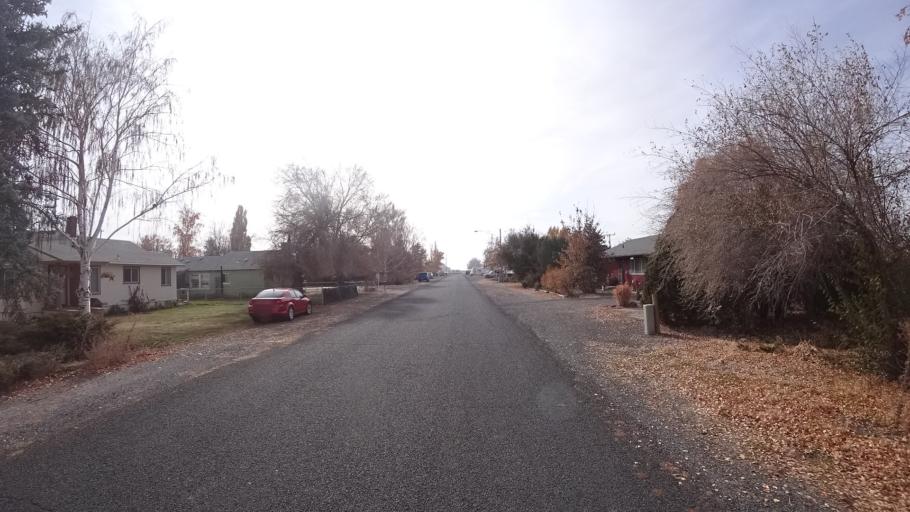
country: US
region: California
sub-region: Siskiyou County
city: Tulelake
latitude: 41.9529
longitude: -121.4809
